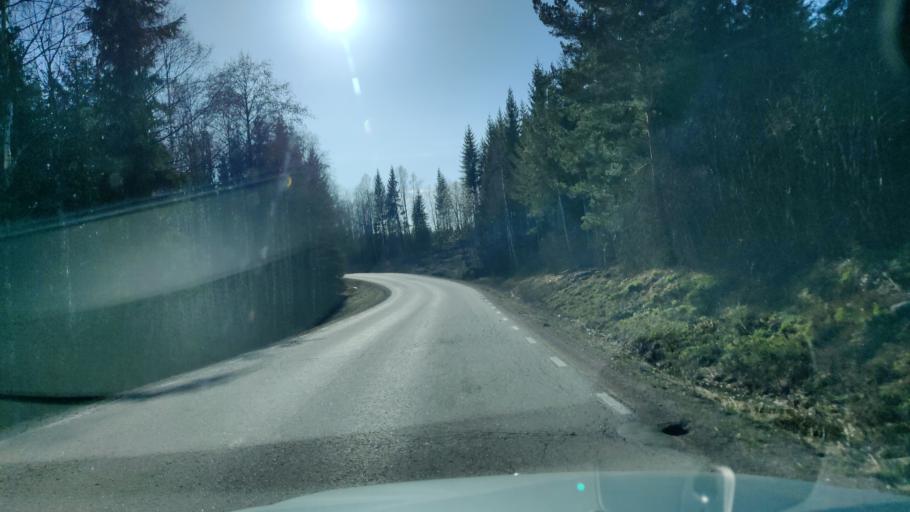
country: SE
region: Vaermland
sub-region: Munkfors Kommun
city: Munkfors
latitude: 59.9850
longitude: 13.3862
